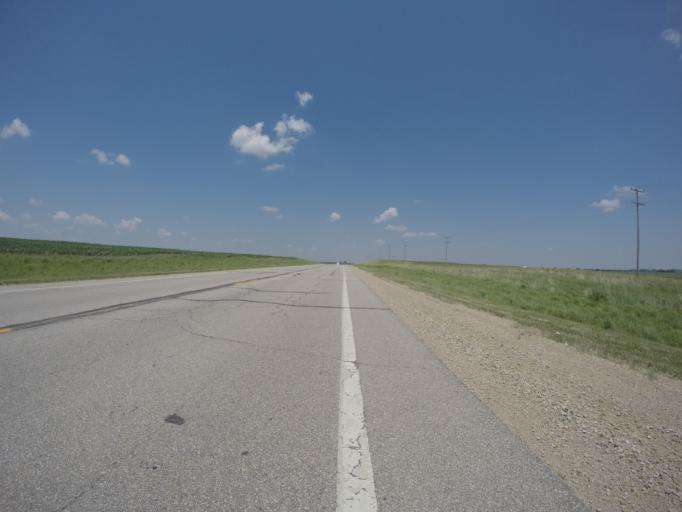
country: US
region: Kansas
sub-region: Doniphan County
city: Troy
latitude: 39.7500
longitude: -95.1438
